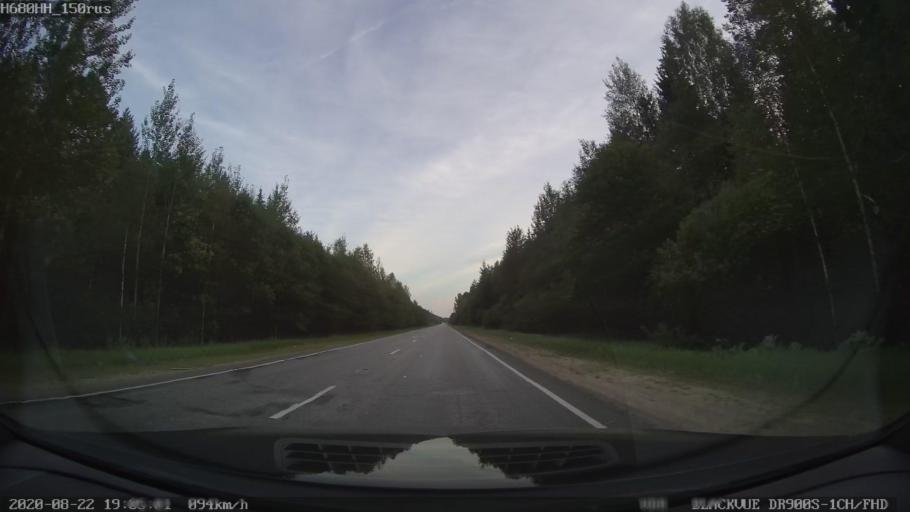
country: RU
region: Tverskaya
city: Sakharovo
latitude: 57.0823
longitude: 36.1137
